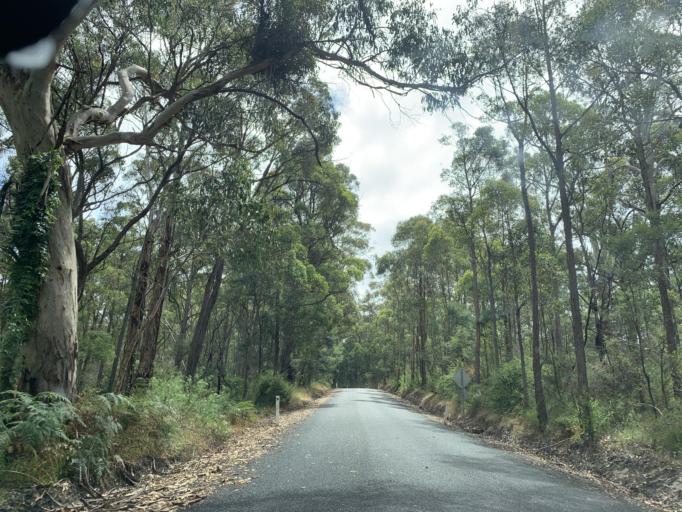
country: AU
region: Victoria
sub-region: Latrobe
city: Traralgon
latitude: -38.1114
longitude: 146.5454
